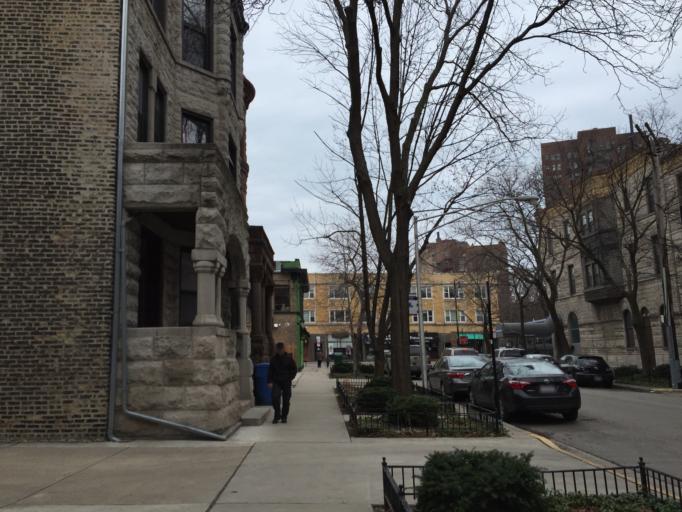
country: US
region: Illinois
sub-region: Cook County
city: Chicago
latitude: 41.9268
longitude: -87.6423
